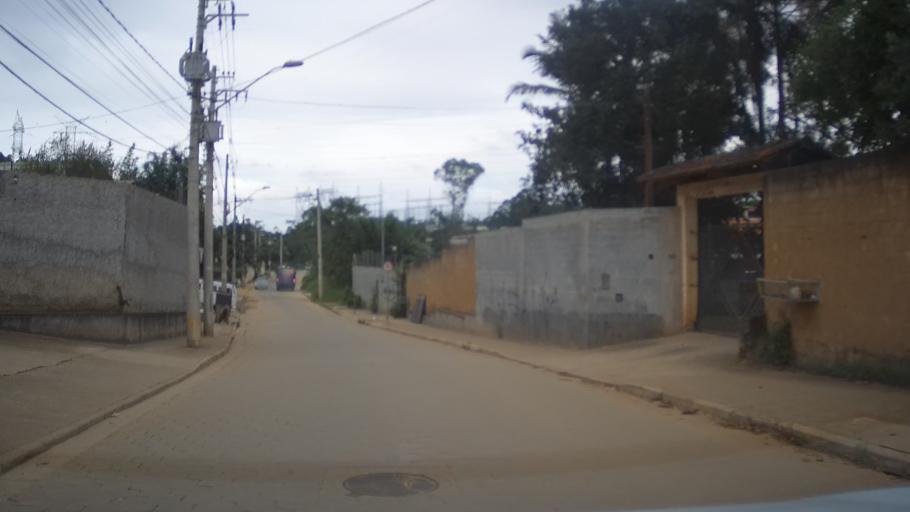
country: BR
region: Sao Paulo
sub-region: Aruja
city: Aruja
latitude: -23.3687
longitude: -46.4018
